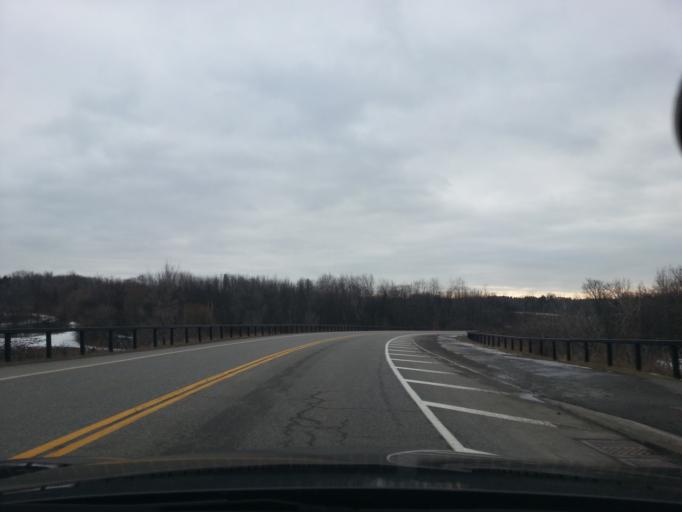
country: CA
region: Quebec
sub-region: Outaouais
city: Gatineau
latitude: 45.4581
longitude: -75.5735
